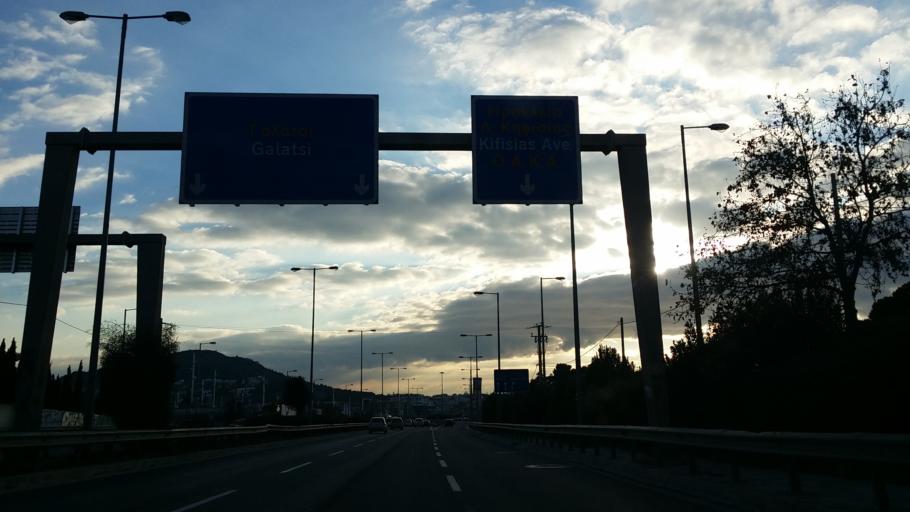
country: GR
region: Attica
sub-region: Nomarchia Athinas
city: Irakleio
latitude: 38.0434
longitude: 23.7799
